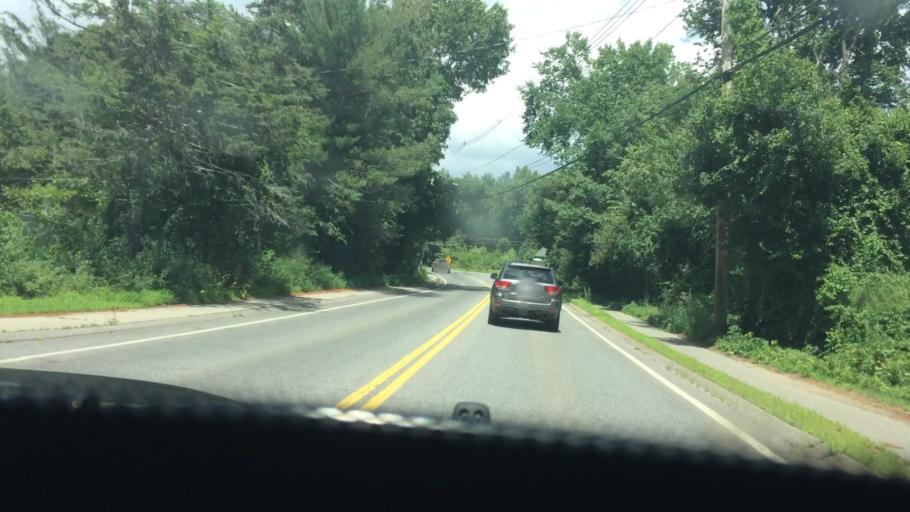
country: US
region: Massachusetts
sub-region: Middlesex County
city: Sudbury
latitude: 42.3985
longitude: -71.4316
